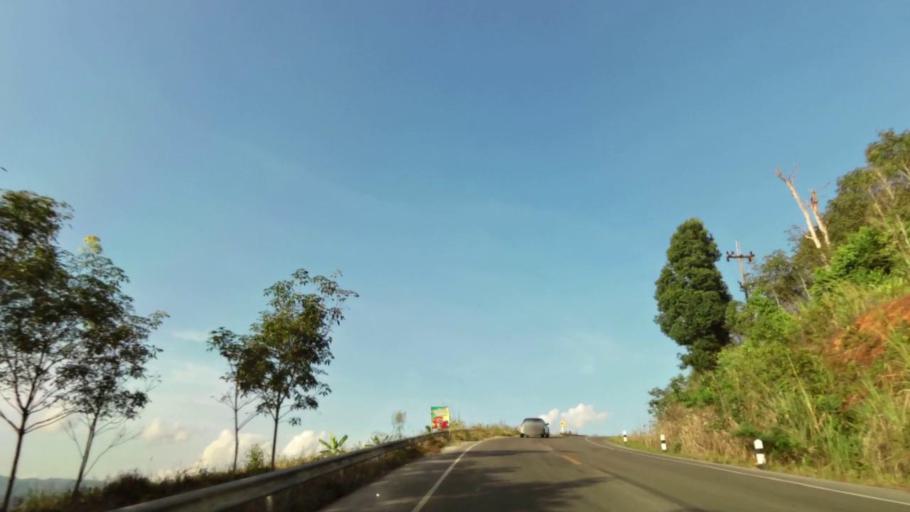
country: TH
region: Chiang Rai
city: Khun Tan
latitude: 19.8652
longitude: 100.4197
